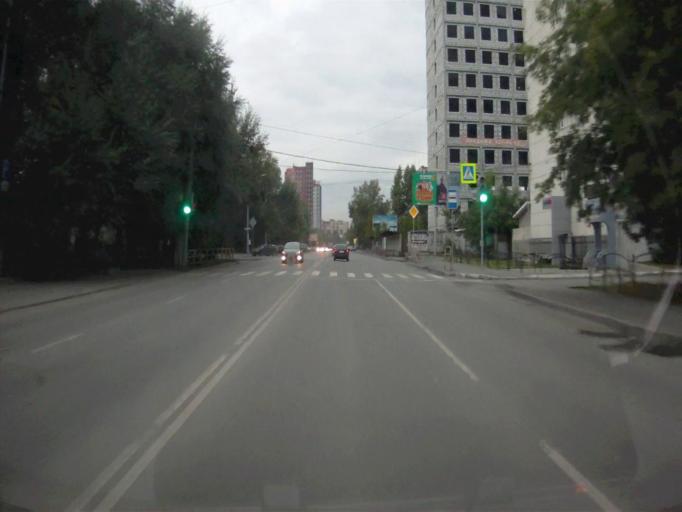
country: RU
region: Chelyabinsk
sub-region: Gorod Chelyabinsk
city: Chelyabinsk
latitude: 55.1473
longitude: 61.3987
